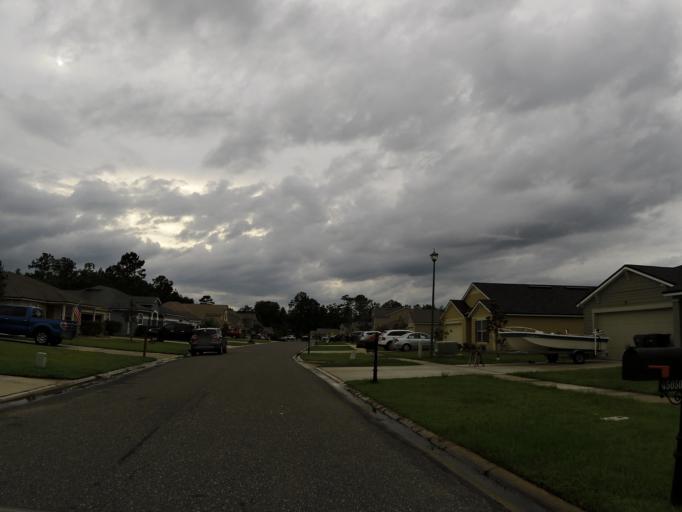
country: US
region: Florida
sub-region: Nassau County
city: Callahan
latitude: 30.5704
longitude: -81.8303
